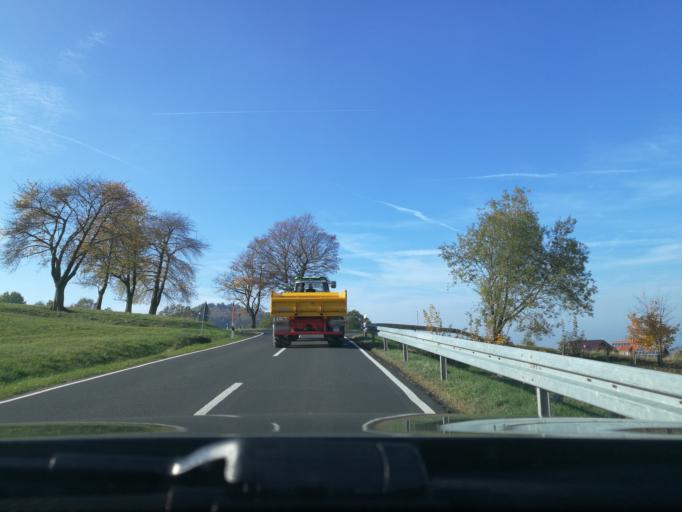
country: DE
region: Hesse
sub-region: Regierungsbezirk Kassel
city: Poppenhausen
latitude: 50.4749
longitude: 9.8715
